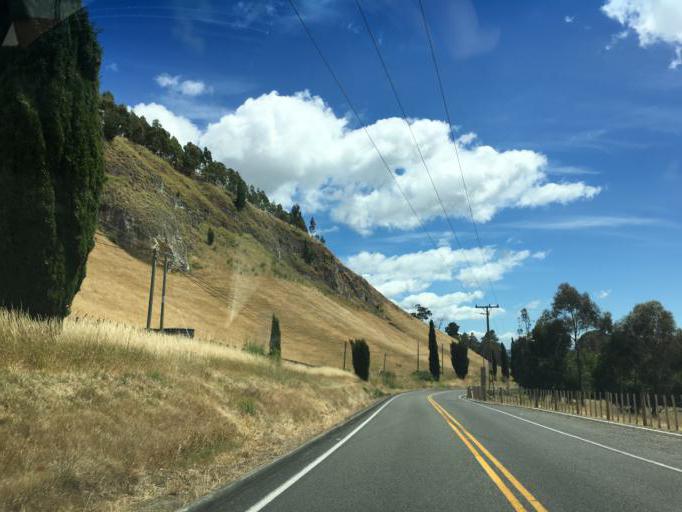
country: NZ
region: Hawke's Bay
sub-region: Hastings District
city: Hastings
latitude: -39.6785
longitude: 176.9217
